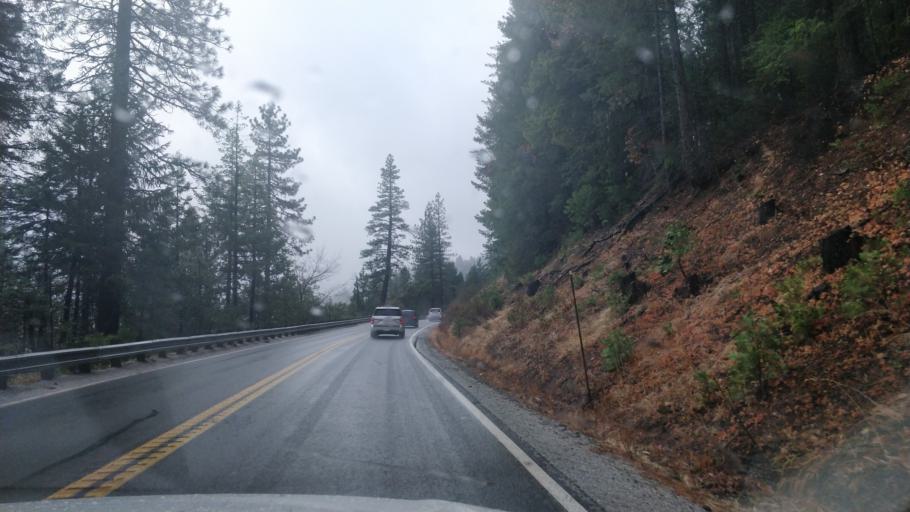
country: US
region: California
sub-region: Nevada County
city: Nevada City
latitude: 39.3201
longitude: -120.8200
